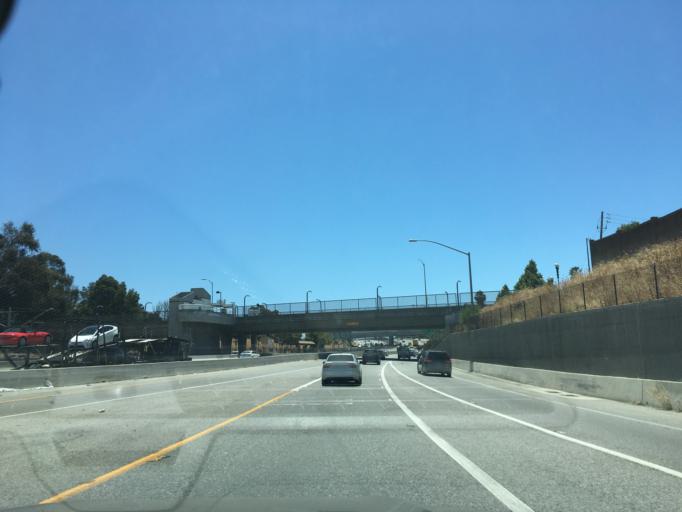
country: US
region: California
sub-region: Santa Clara County
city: San Jose
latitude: 37.3209
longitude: -121.8910
